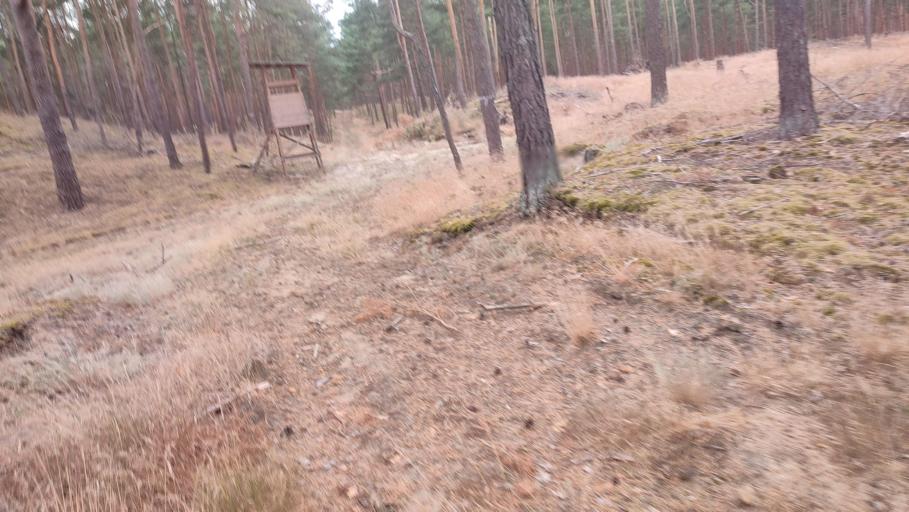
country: DE
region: Lower Saxony
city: Hitzacker
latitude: 53.1998
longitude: 11.0717
